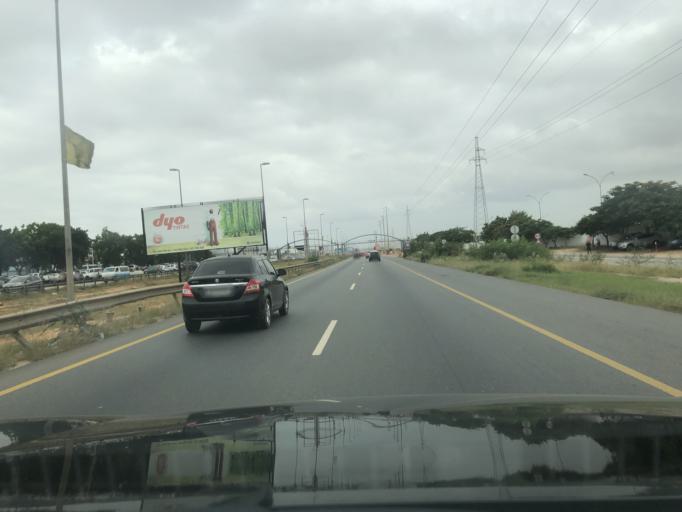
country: AO
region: Luanda
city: Luanda
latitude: -8.9733
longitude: 13.2357
